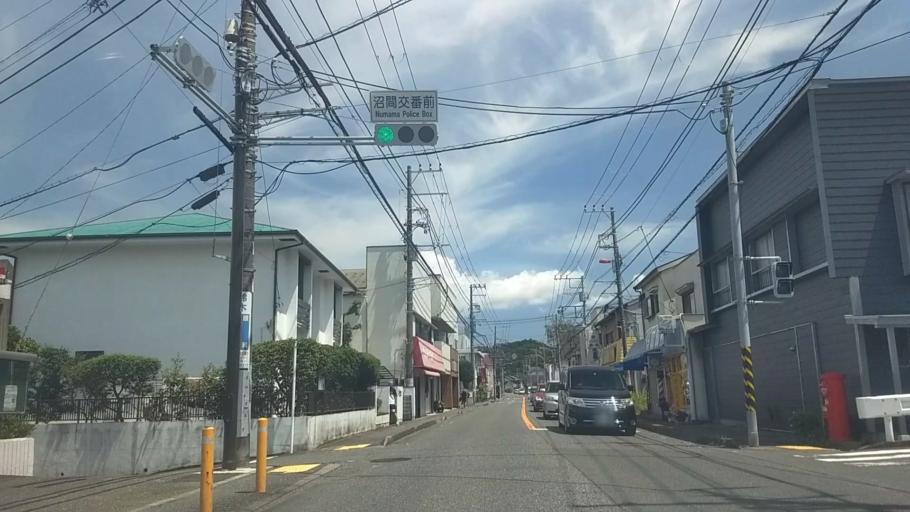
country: JP
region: Kanagawa
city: Zushi
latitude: 35.2971
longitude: 139.6045
